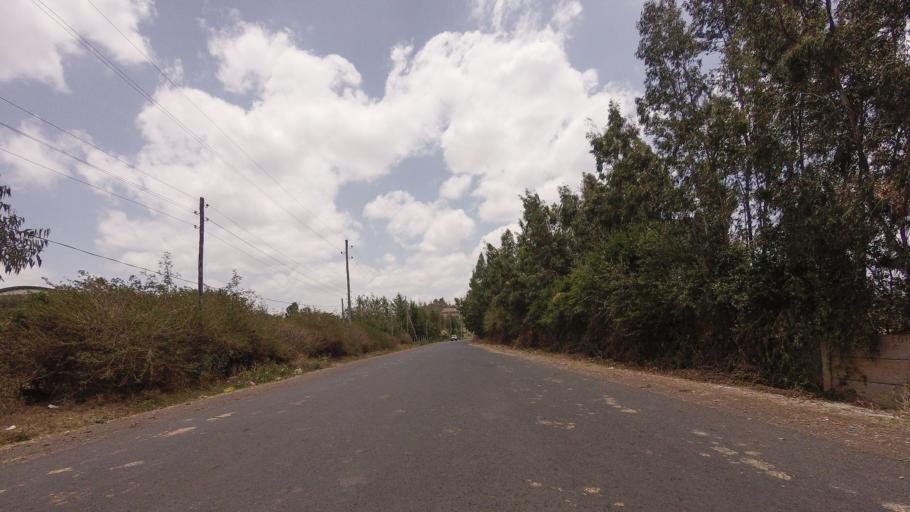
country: ET
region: Oromiya
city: Bishoftu
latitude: 8.7782
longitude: 38.9880
